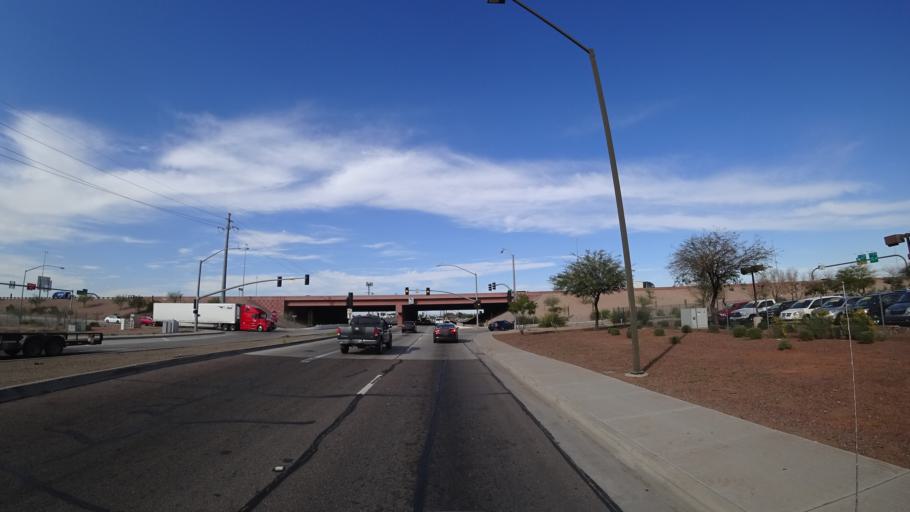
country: US
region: Arizona
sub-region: Maricopa County
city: Tolleson
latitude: 33.4601
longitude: -112.2898
